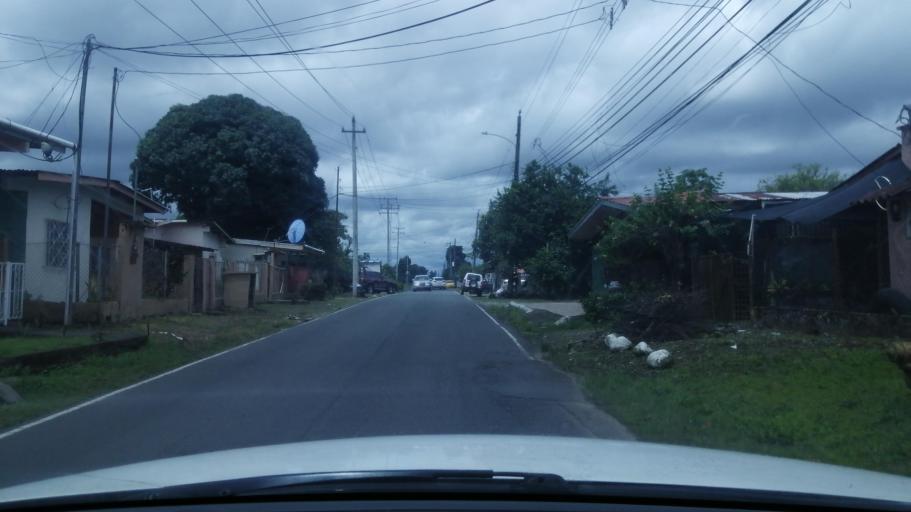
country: PA
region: Chiriqui
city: David
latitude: 8.4289
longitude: -82.4206
